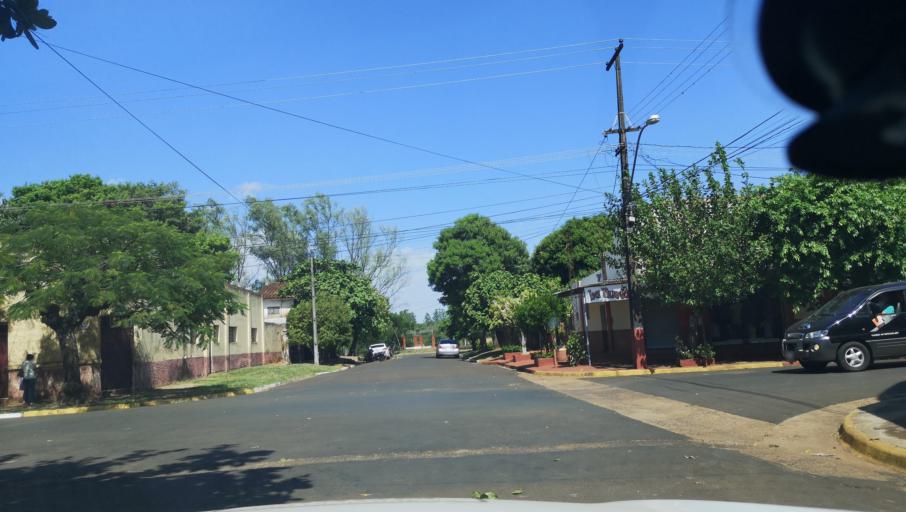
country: PY
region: Itapua
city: Carmen del Parana
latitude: -27.1581
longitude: -56.2390
